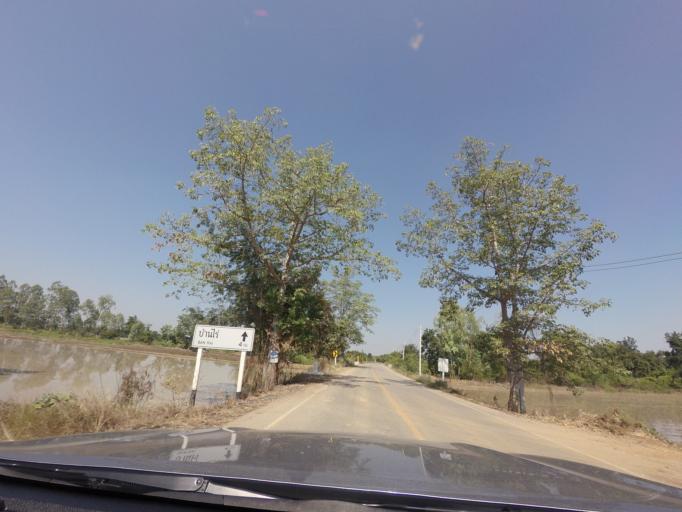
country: TH
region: Sukhothai
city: Si Samrong
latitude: 17.1493
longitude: 99.7696
